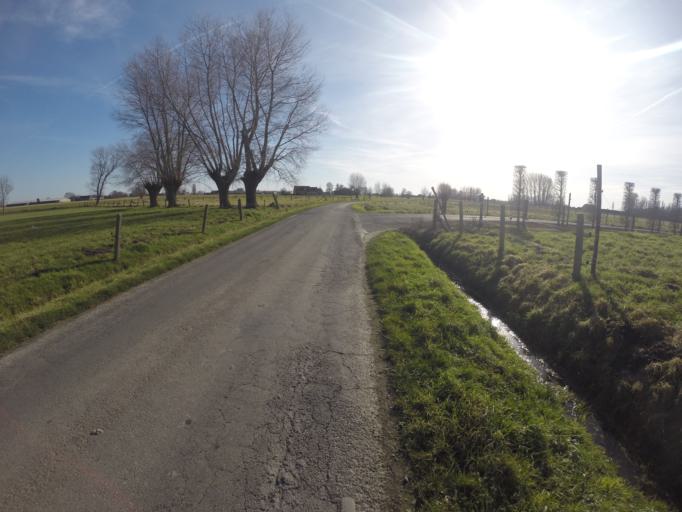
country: BE
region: Flanders
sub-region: Provincie West-Vlaanderen
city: Ruiselede
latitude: 51.0399
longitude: 3.4227
